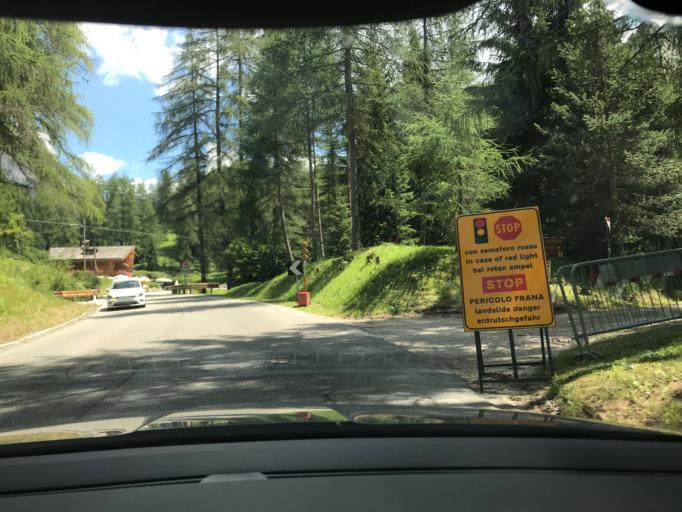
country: IT
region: Veneto
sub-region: Provincia di Belluno
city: Cortina d'Ampezzo
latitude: 46.5443
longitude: 12.1643
